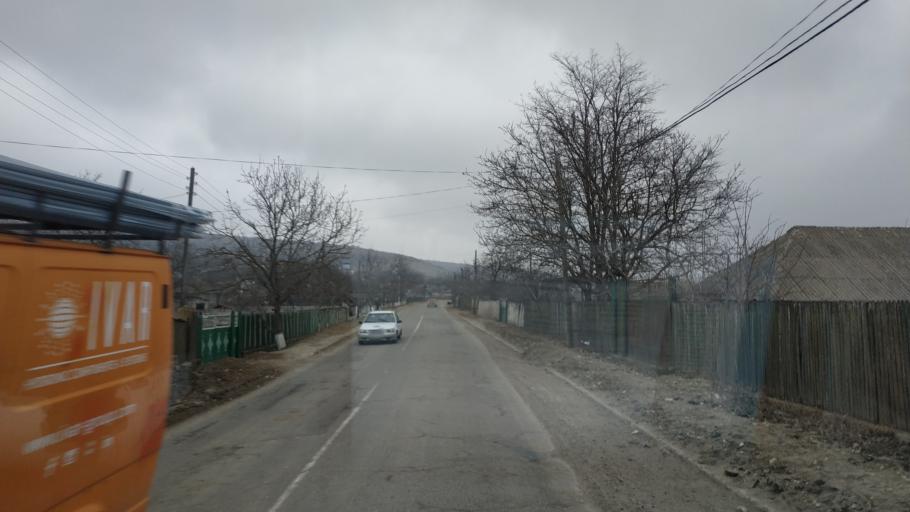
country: MD
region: Hincesti
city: Hincesti
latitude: 46.9795
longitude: 28.4563
